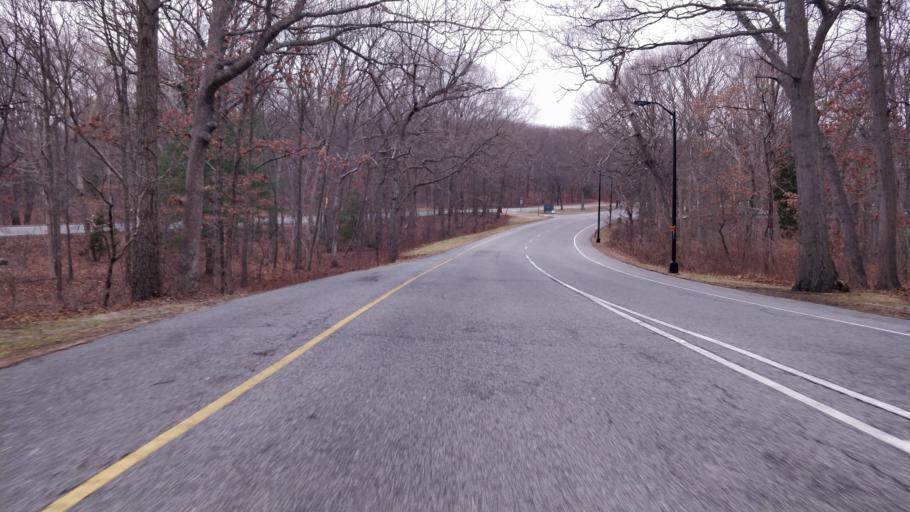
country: US
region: New York
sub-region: Nassau County
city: Brookville
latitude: 40.7966
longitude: -73.5640
